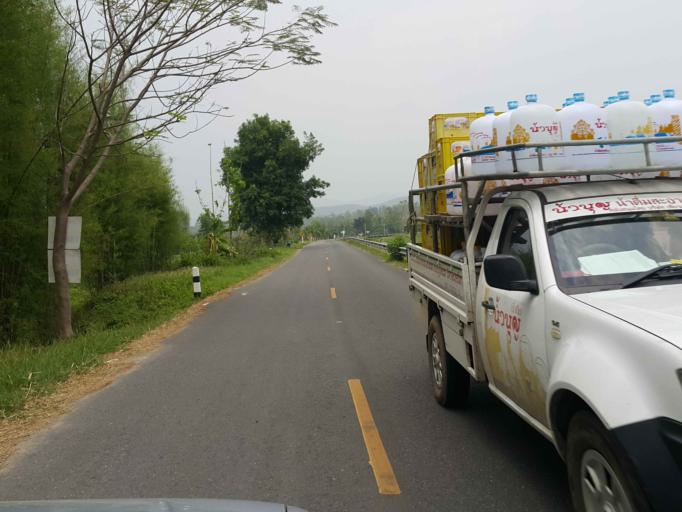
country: TH
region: Chiang Mai
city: San Sai
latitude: 18.9552
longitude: 98.9896
